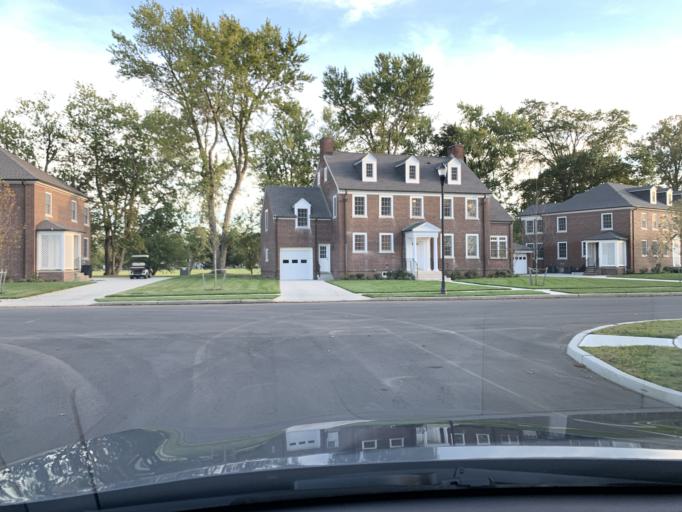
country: US
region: New Jersey
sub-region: Monmouth County
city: Little Silver
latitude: 40.3174
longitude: -74.0418
